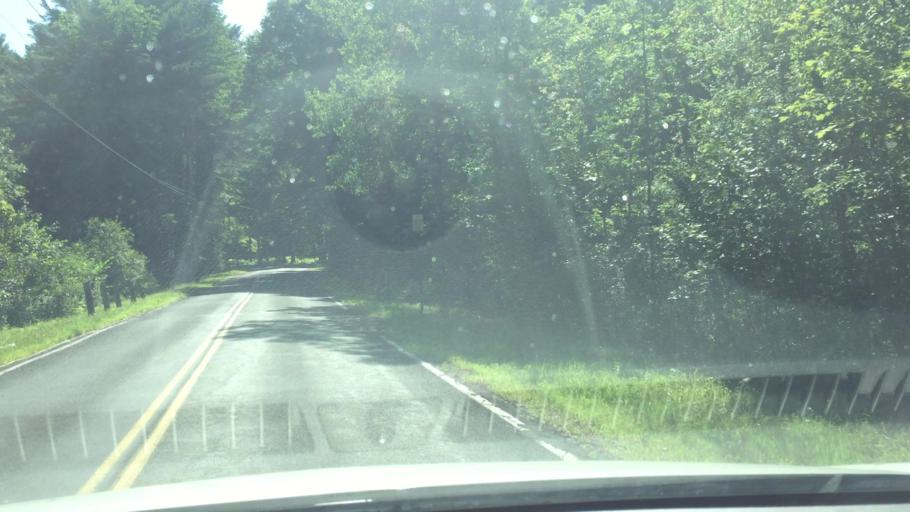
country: US
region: Massachusetts
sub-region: Berkshire County
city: West Stockbridge
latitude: 42.3024
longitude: -73.3751
